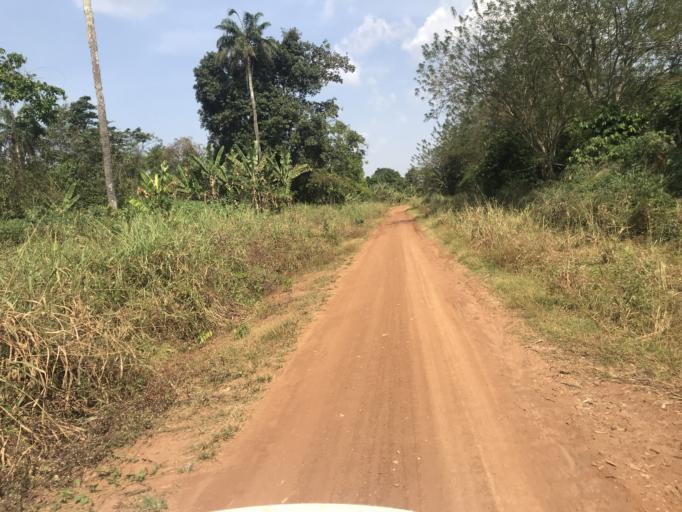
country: NG
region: Osun
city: Osu
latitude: 7.6463
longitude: 4.6584
